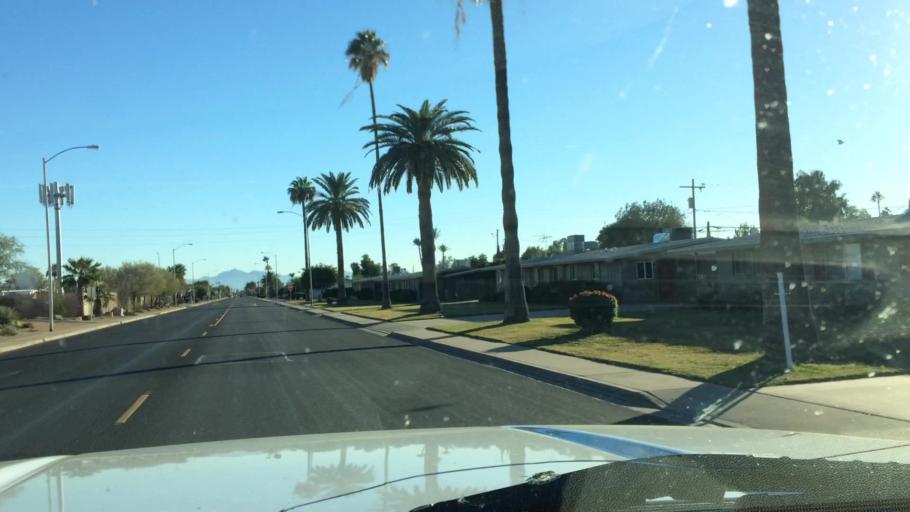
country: US
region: Arizona
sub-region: Maricopa County
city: Sun City
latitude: 33.5962
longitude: -112.2813
